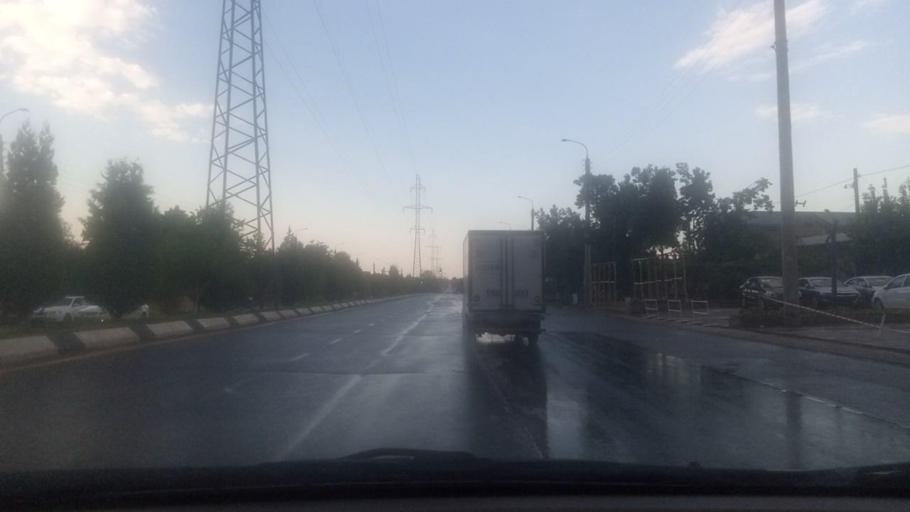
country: UZ
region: Toshkent Shahri
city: Tashkent
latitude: 41.3139
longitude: 69.1933
